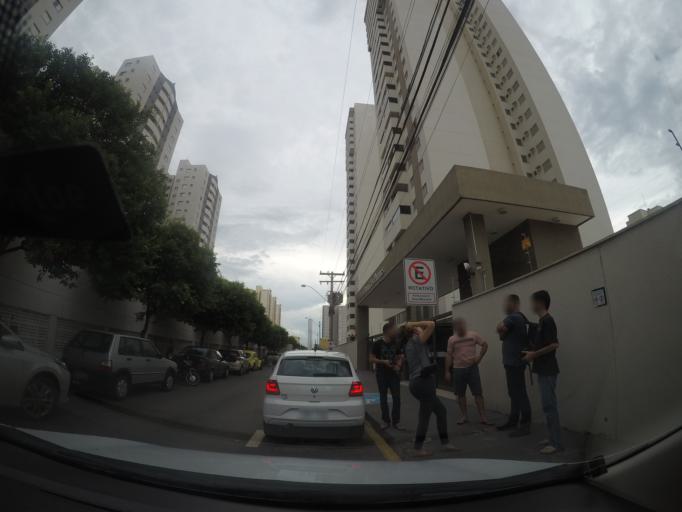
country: BR
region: Goias
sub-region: Goiania
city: Goiania
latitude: -16.6547
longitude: -49.2418
